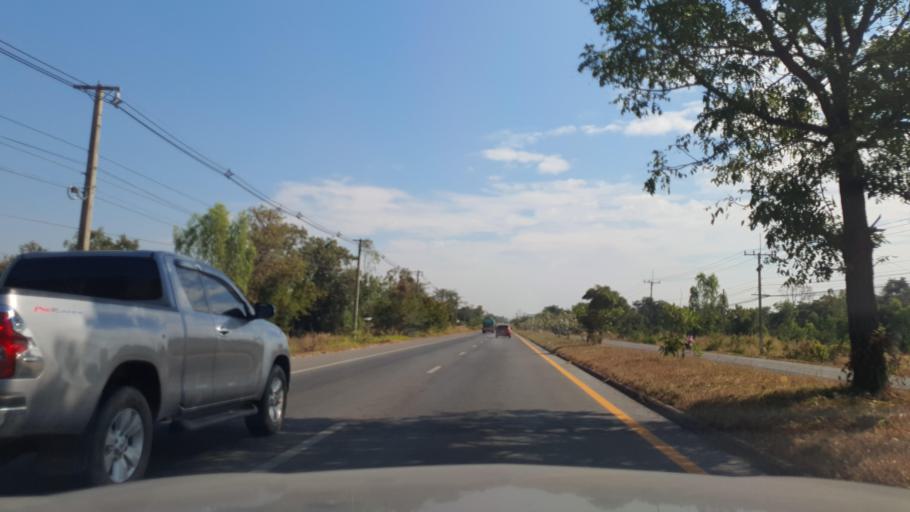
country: TH
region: Maha Sarakham
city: Chiang Yuen
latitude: 16.3806
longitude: 103.2015
